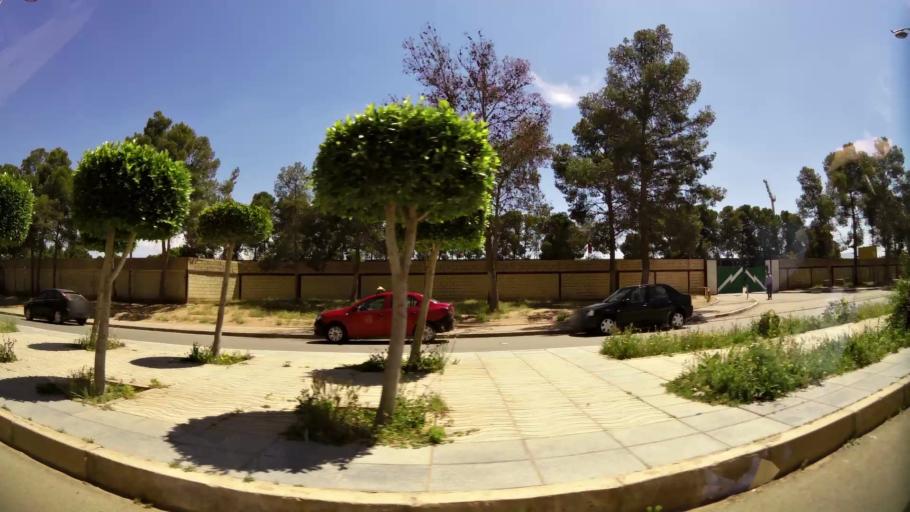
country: MA
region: Oriental
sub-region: Oujda-Angad
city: Oujda
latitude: 34.6594
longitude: -1.9362
